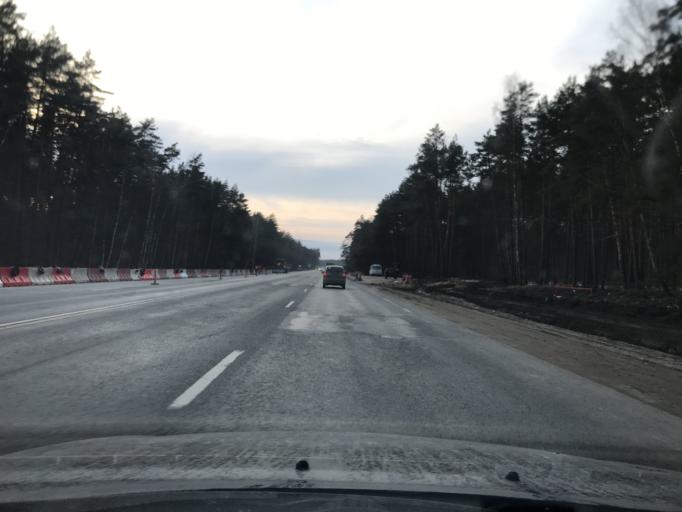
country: RU
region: Kaluga
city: Mstikhino
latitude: 54.5793
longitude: 36.0926
